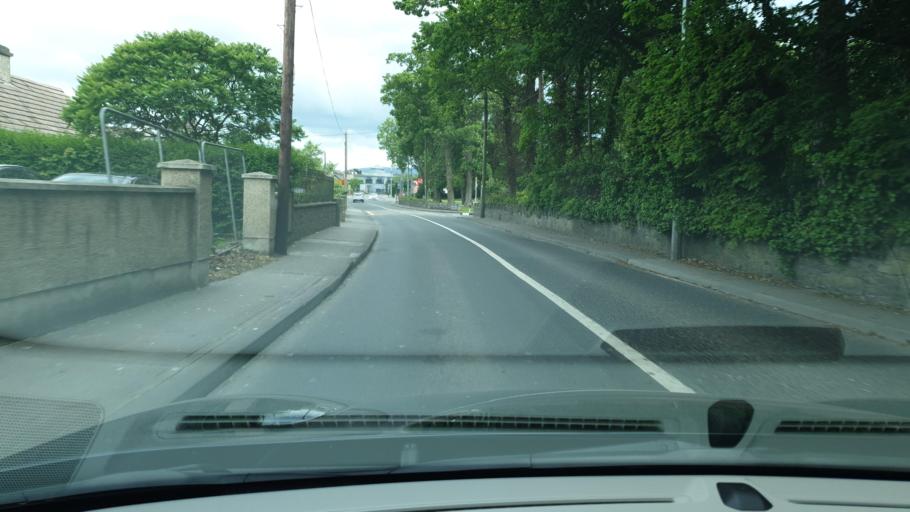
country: IE
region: Leinster
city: Clondalkin
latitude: 53.3312
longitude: -6.3993
